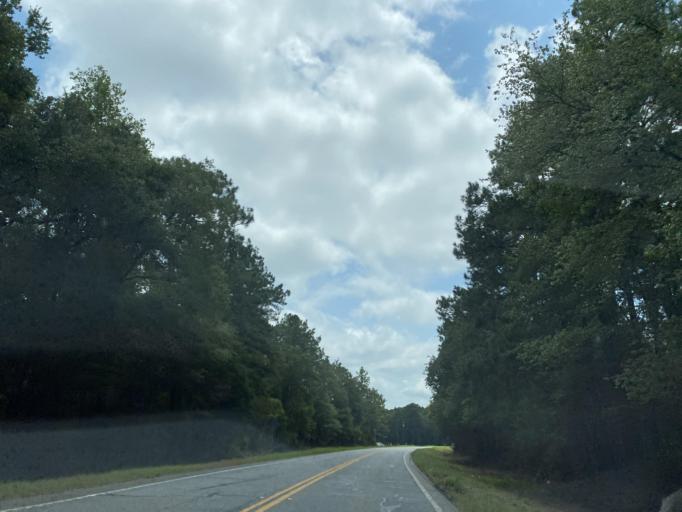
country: US
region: Georgia
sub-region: Wheeler County
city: Alamo
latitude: 32.1363
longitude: -82.7841
